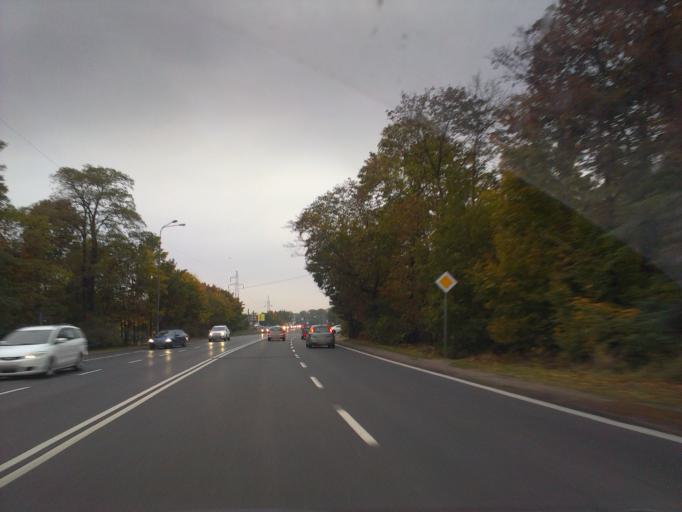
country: PL
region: Greater Poland Voivodeship
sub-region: Poznan
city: Poznan
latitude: 52.4430
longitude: 16.9181
